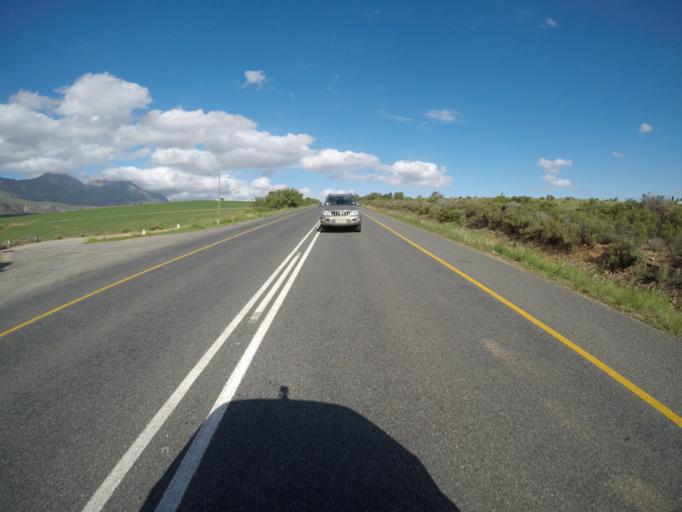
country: ZA
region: Western Cape
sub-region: Cape Winelands District Municipality
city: Ashton
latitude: -33.9526
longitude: 20.2299
